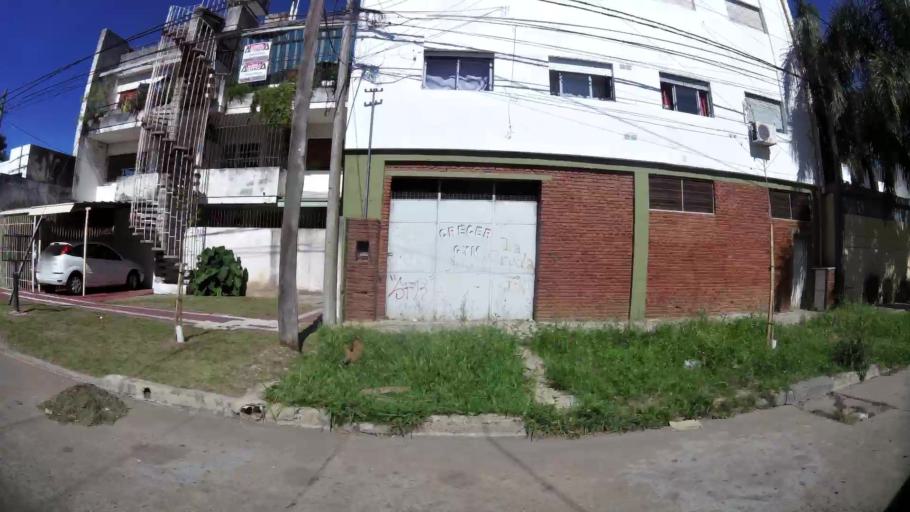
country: AR
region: Santa Fe
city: Santa Fe de la Vera Cruz
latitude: -31.6156
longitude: -60.6732
